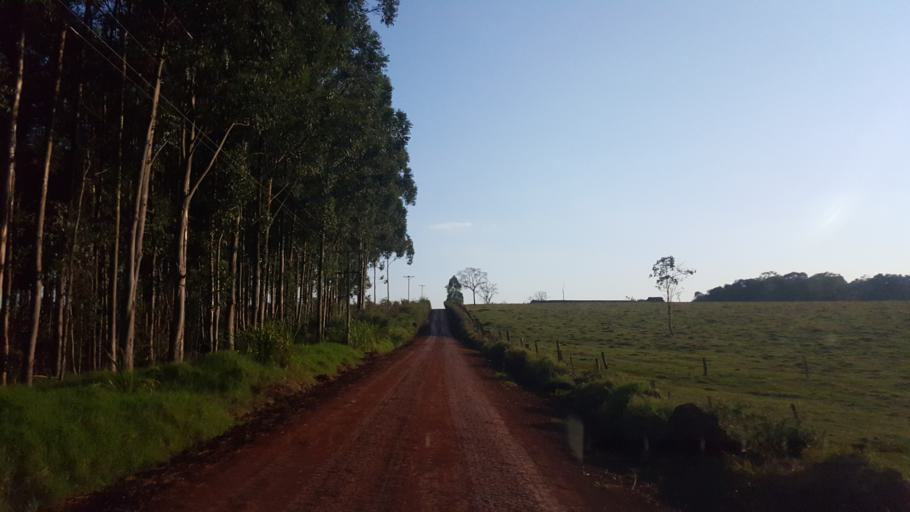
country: AR
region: Misiones
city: Capiovi
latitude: -26.9101
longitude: -55.0509
